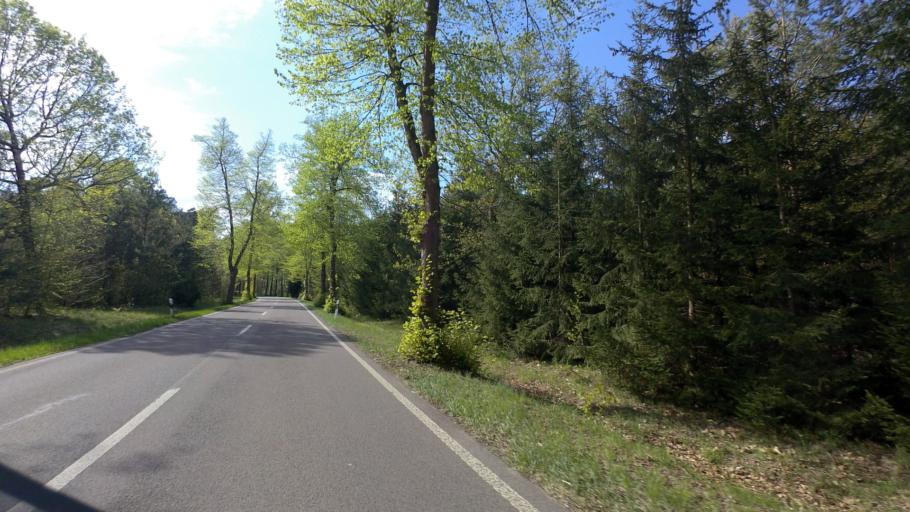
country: DE
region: Brandenburg
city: Milmersdorf
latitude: 53.0026
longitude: 13.5835
